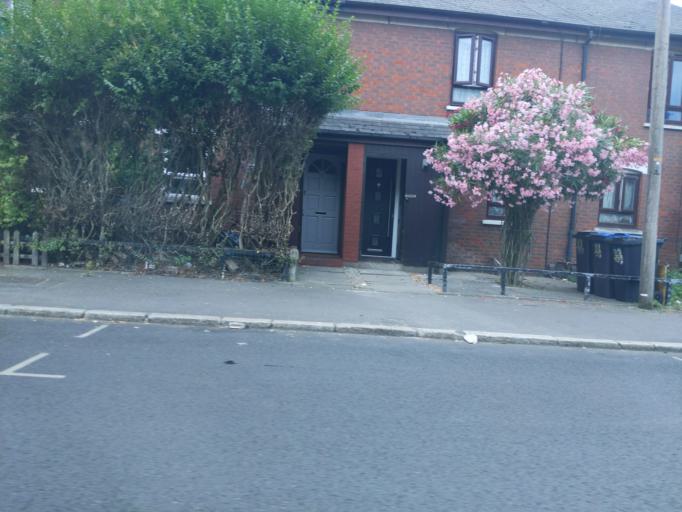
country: GB
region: England
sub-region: Greater London
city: Croydon
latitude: 51.3861
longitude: -0.1010
